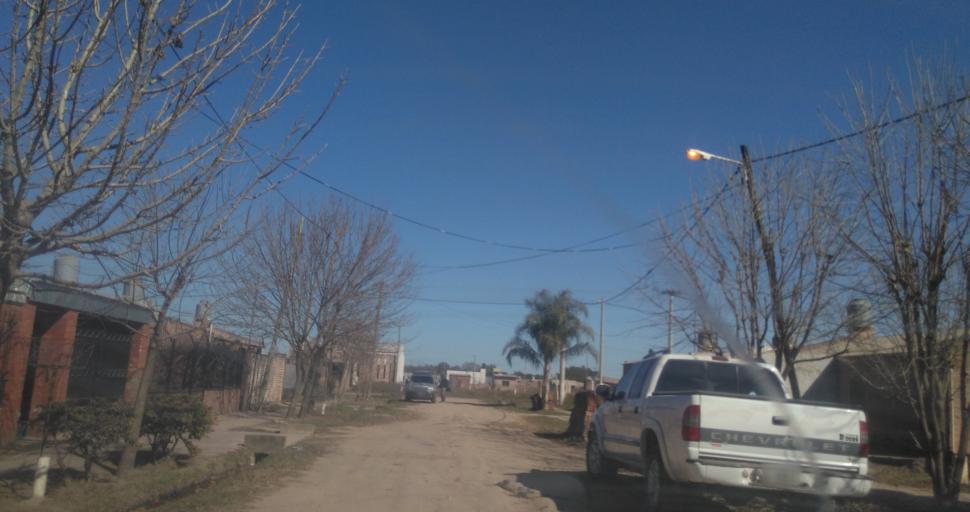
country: AR
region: Chaco
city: Fontana
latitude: -27.4572
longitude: -59.0441
